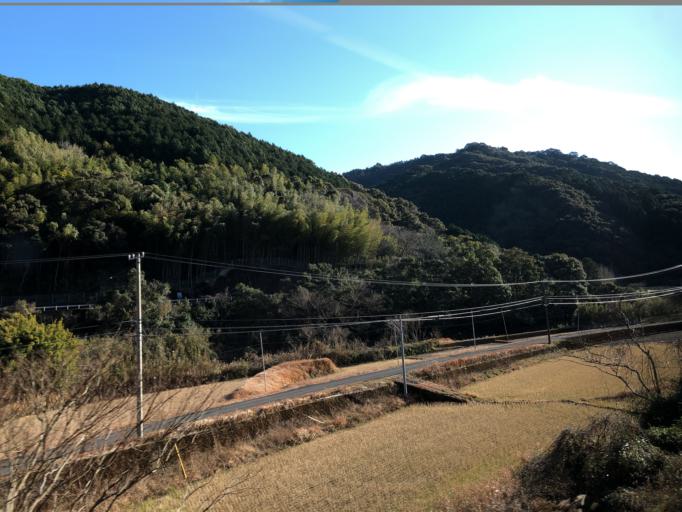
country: JP
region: Kochi
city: Nakamura
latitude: 33.1124
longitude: 133.1112
